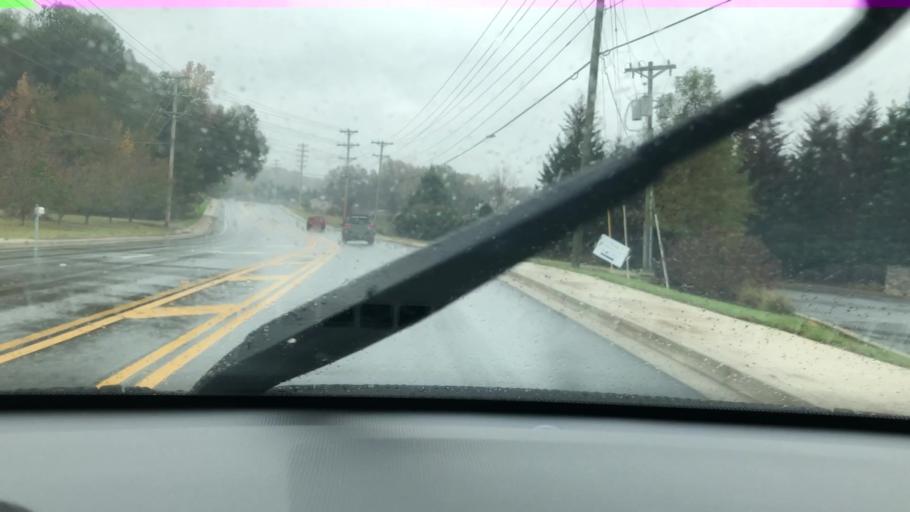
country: US
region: South Carolina
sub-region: Greenville County
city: Five Forks
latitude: 34.8328
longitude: -82.2709
